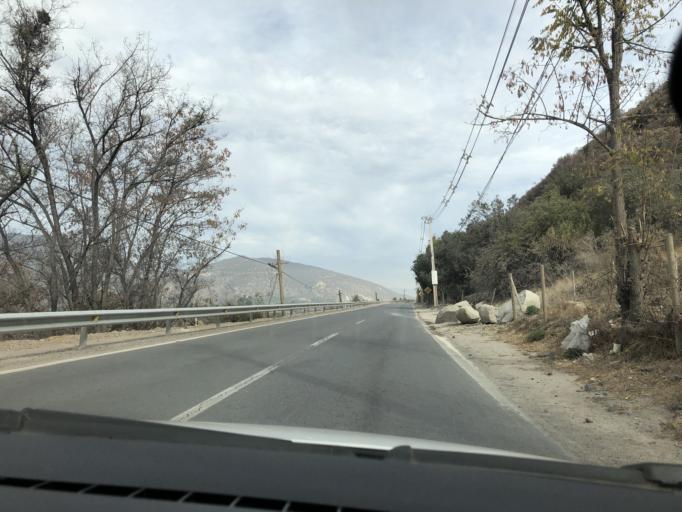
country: CL
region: Santiago Metropolitan
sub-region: Provincia de Cordillera
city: Puente Alto
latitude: -33.5958
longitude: -70.4918
